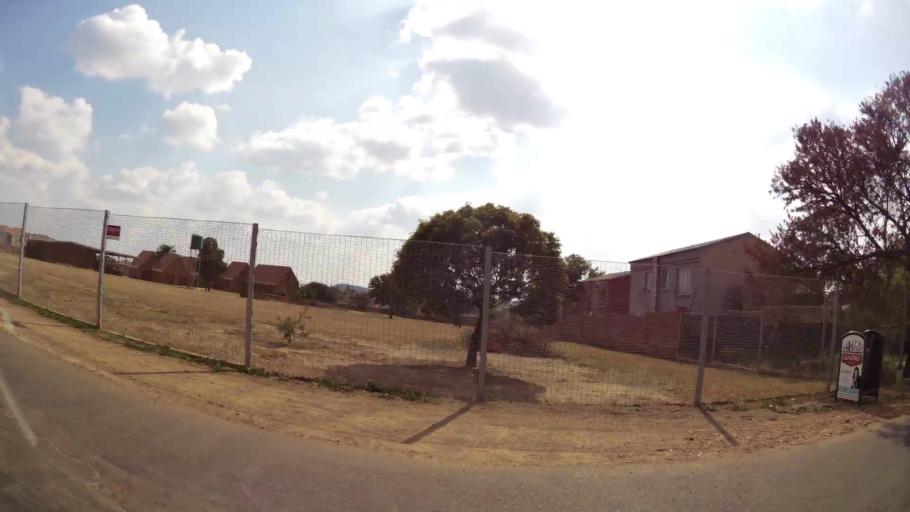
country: ZA
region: Gauteng
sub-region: City of Tshwane Metropolitan Municipality
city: Centurion
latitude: -25.8093
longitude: 28.3482
